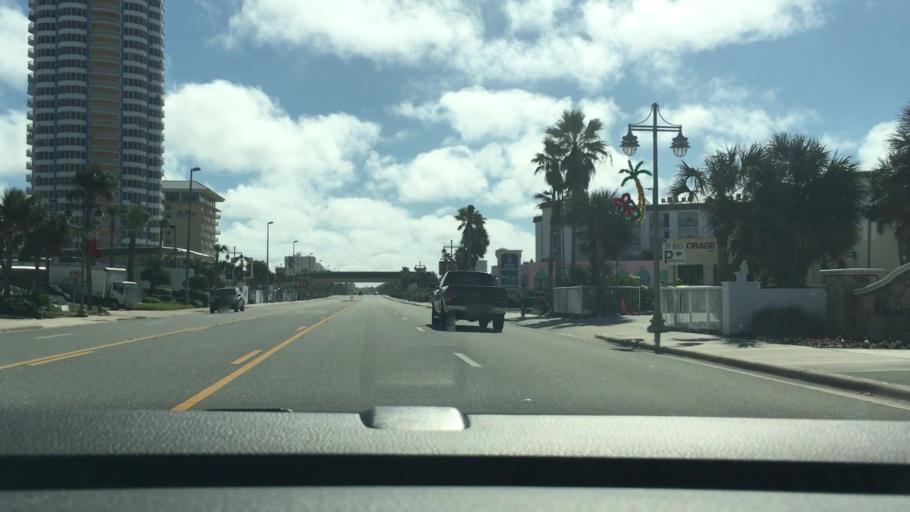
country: US
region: Florida
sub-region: Volusia County
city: Daytona Beach Shores
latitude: 29.1834
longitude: -80.9866
